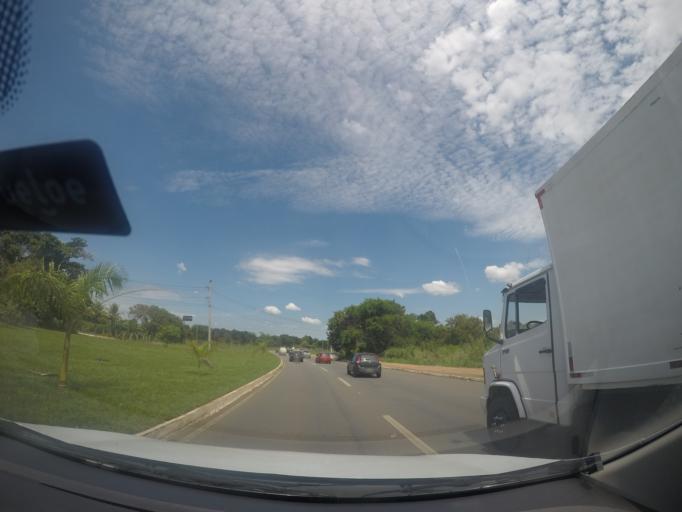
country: BR
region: Goias
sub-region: Goiania
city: Goiania
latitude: -16.6825
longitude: -49.3340
